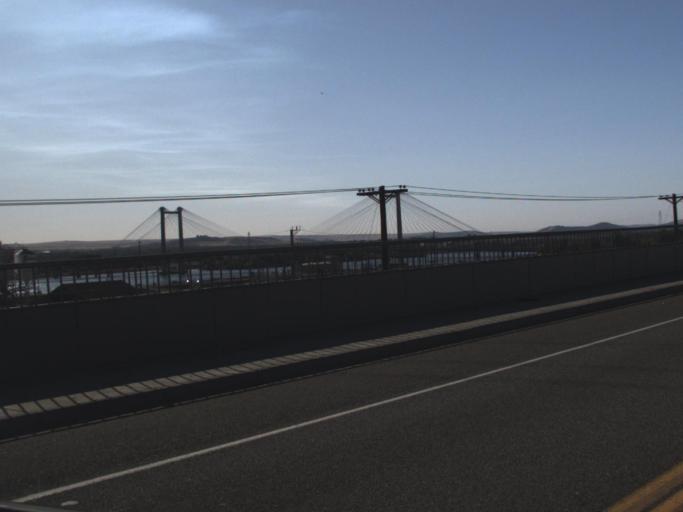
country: US
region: Washington
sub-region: Franklin County
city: Pasco
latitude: 46.2216
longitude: -119.0913
